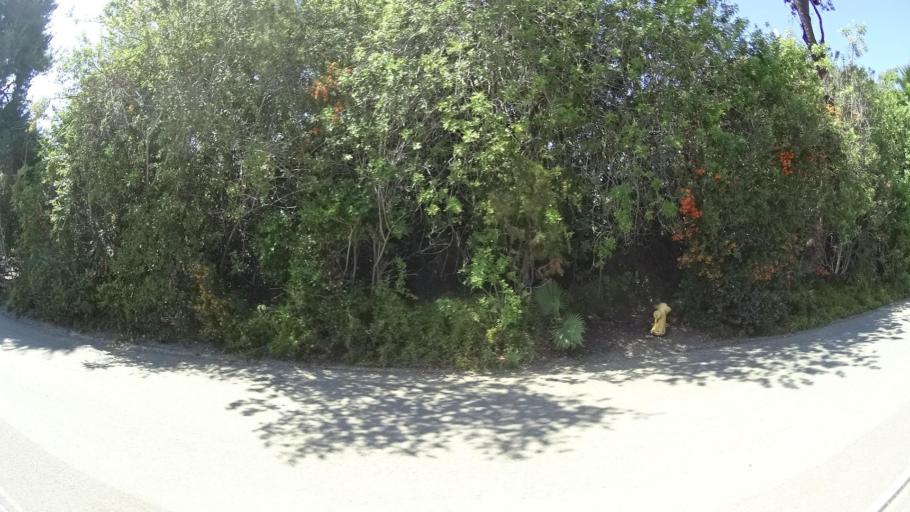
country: US
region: California
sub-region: San Diego County
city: Rancho Santa Fe
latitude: 33.0172
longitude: -117.1934
